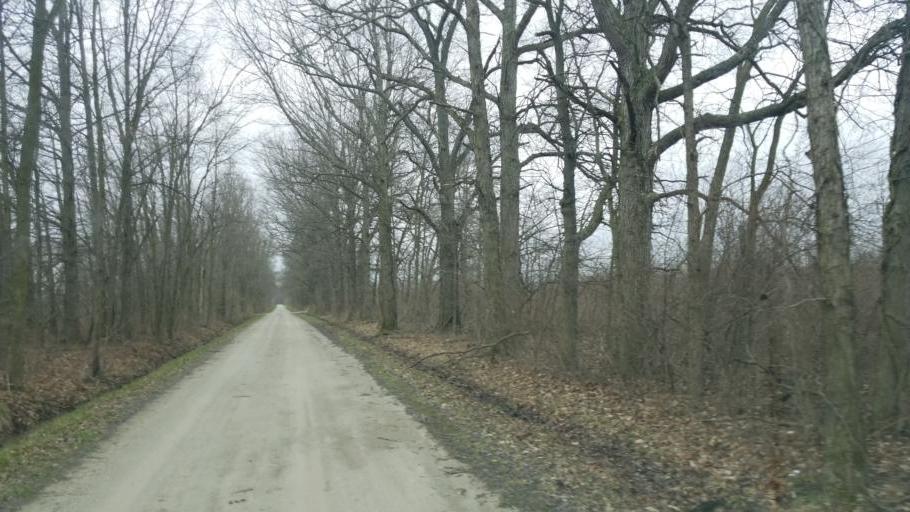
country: US
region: Ohio
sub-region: Wyandot County
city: Upper Sandusky
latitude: 40.7149
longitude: -83.3430
